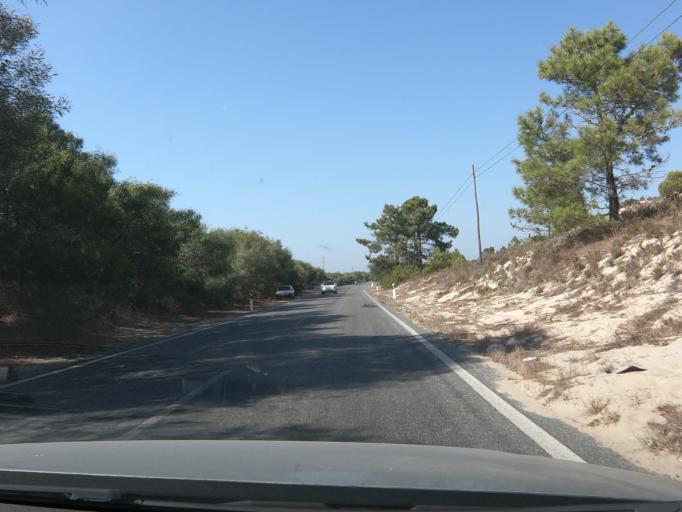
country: PT
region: Setubal
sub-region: Setubal
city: Setubal
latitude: 38.3959
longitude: -8.8046
